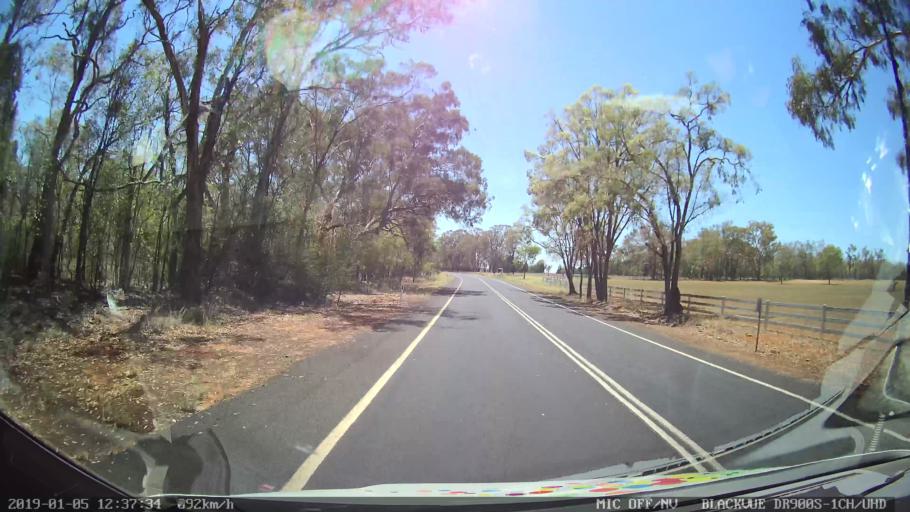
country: AU
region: New South Wales
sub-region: Warrumbungle Shire
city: Coonabarabran
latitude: -31.2026
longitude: 149.4567
